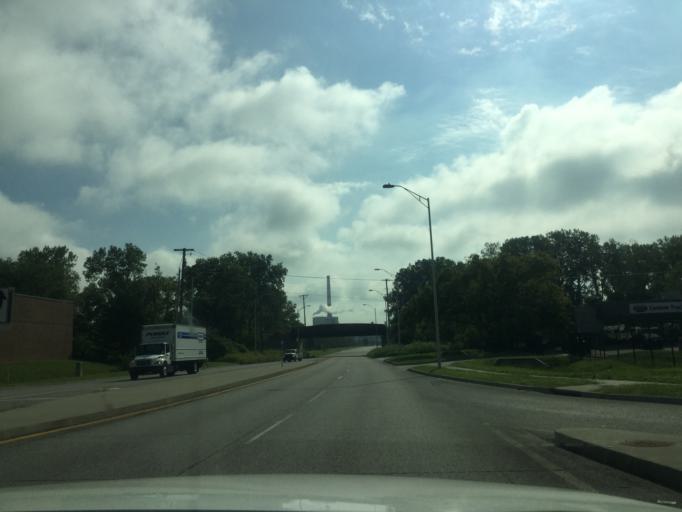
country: US
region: Missouri
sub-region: Jackson County
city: Sugar Creek
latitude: 39.1299
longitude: -94.4965
